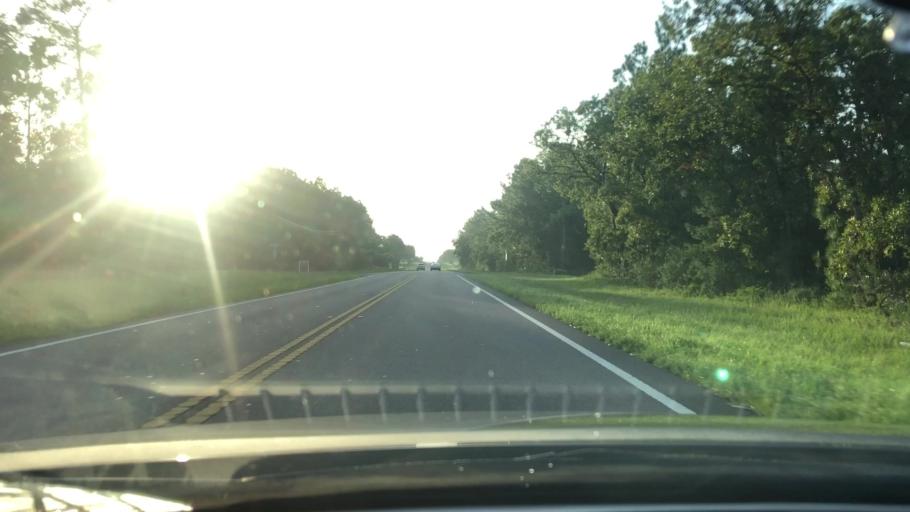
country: US
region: Florida
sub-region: Marion County
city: Belleview
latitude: 29.0261
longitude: -82.2227
